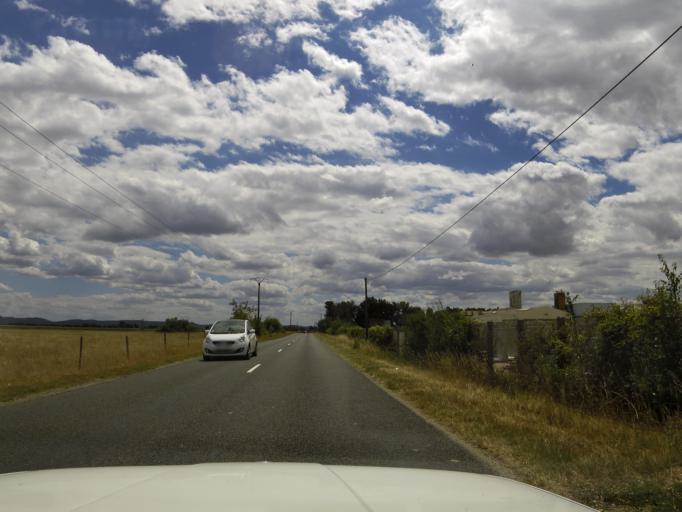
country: FR
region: Rhone-Alpes
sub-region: Departement de l'Ain
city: Saint-Maurice-de-Gourdans
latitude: 45.8084
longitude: 5.2140
